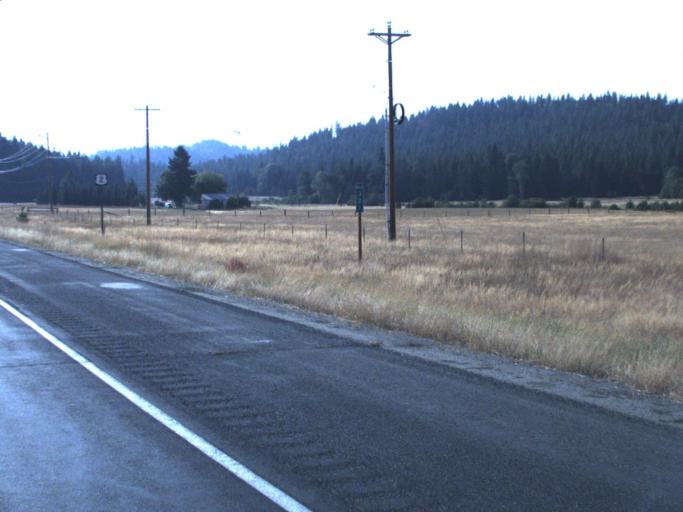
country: US
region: Washington
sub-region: Spokane County
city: Deer Park
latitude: 48.0969
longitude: -117.2852
